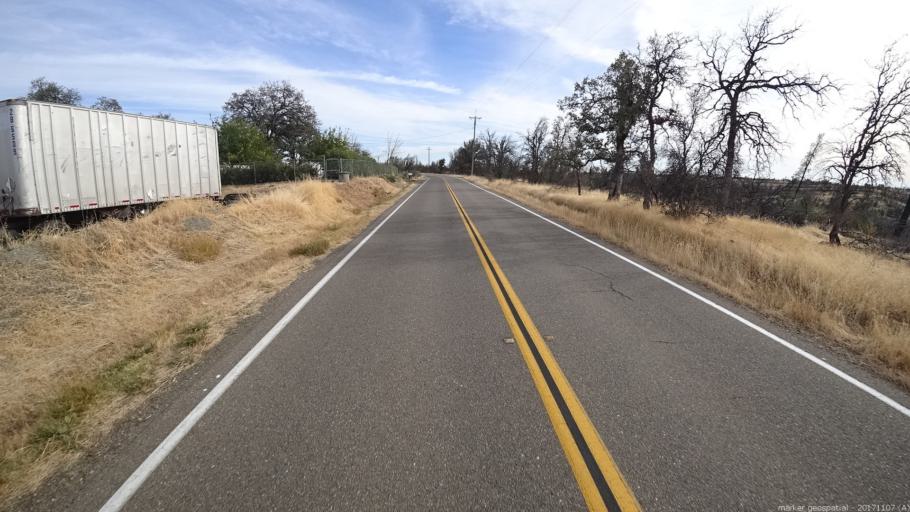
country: US
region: California
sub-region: Shasta County
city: Shasta
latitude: 40.4838
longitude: -122.5091
